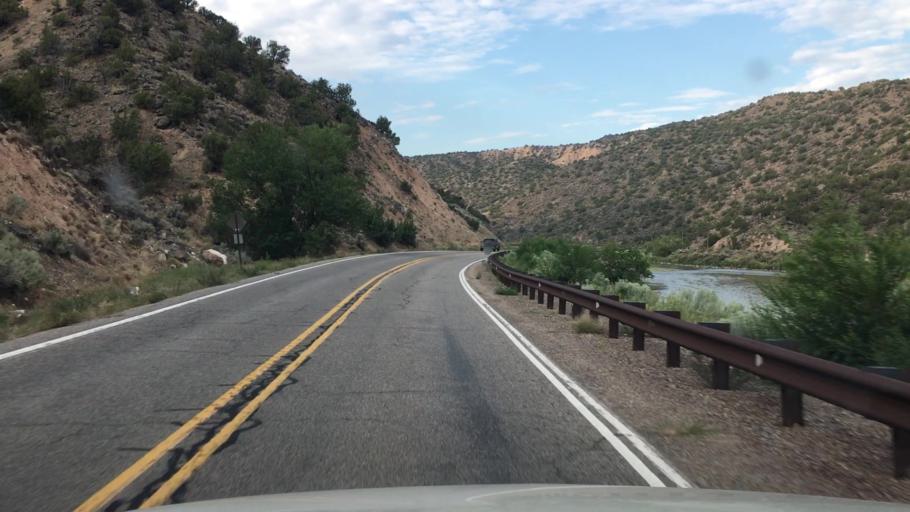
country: US
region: New Mexico
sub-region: Rio Arriba County
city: Ohkay Owingeh
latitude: 36.1915
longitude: -105.9780
